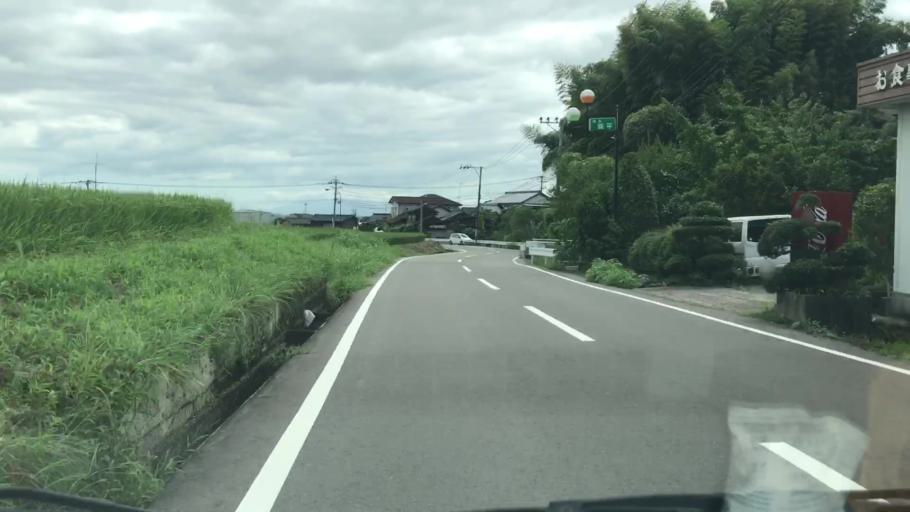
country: JP
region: Saga Prefecture
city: Takeocho-takeo
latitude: 33.2305
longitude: 130.1448
